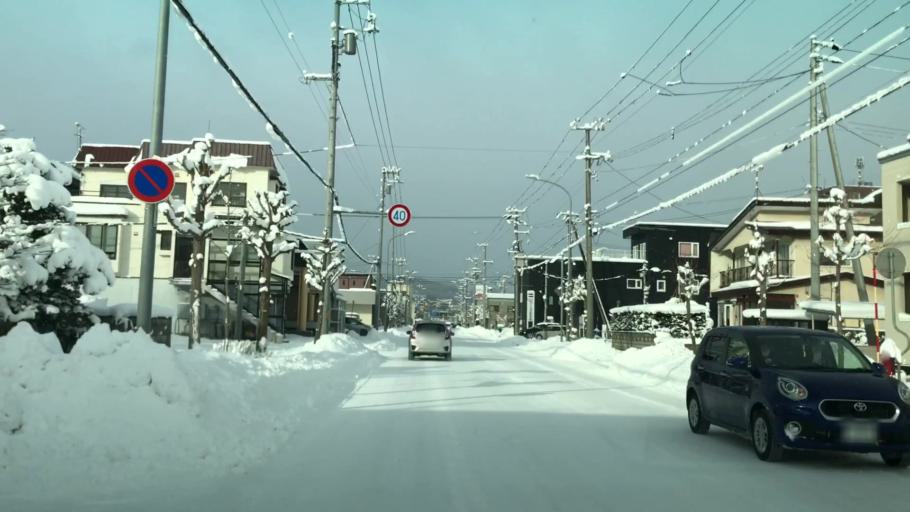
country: JP
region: Hokkaido
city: Yoichi
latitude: 43.1833
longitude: 140.7982
